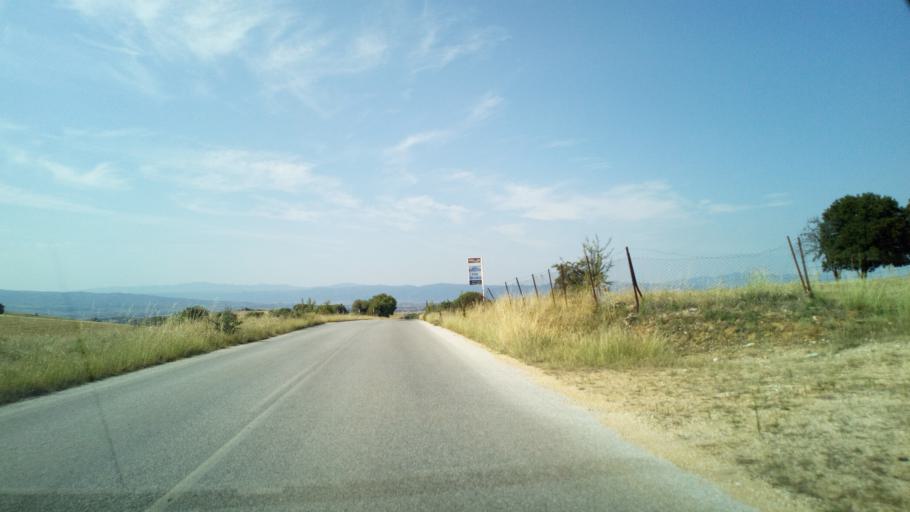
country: GR
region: Central Macedonia
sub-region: Nomos Thessalonikis
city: Nea Apollonia
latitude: 40.5128
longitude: 23.4737
